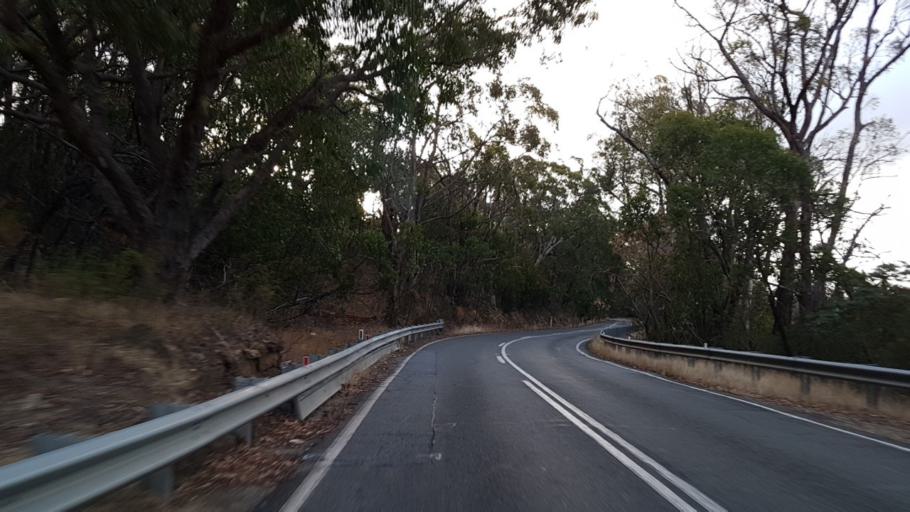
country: AU
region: South Australia
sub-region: Adelaide Hills
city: Crafers
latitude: -34.9577
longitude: 138.7078
